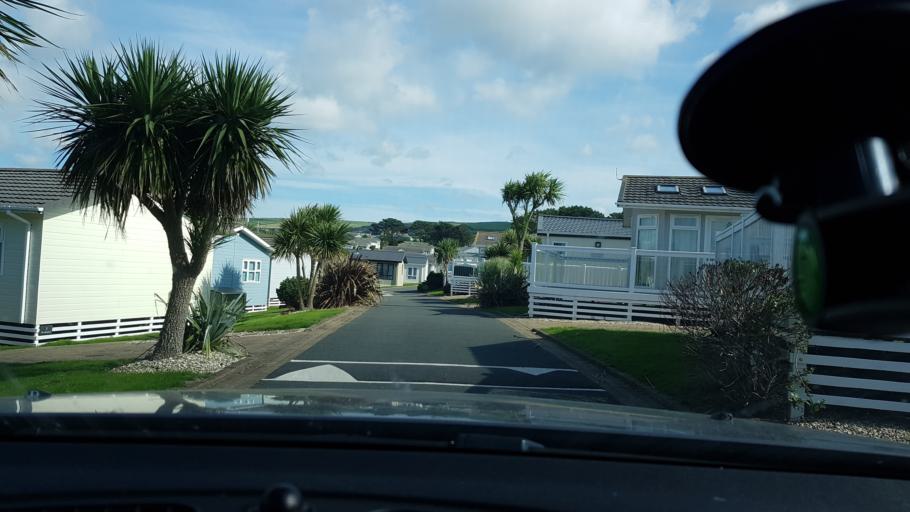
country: GB
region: England
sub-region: Cornwall
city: Tintagel
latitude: 50.6692
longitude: -4.7424
